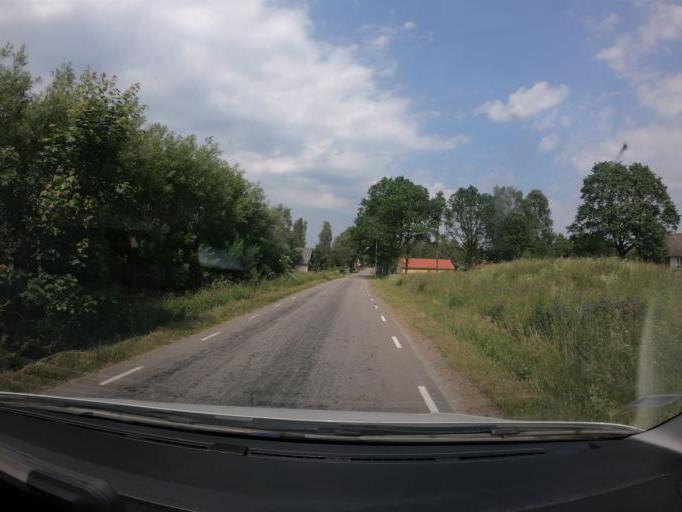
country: SE
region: Skane
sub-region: Hassleholms Kommun
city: Bjarnum
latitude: 56.3122
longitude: 13.5876
